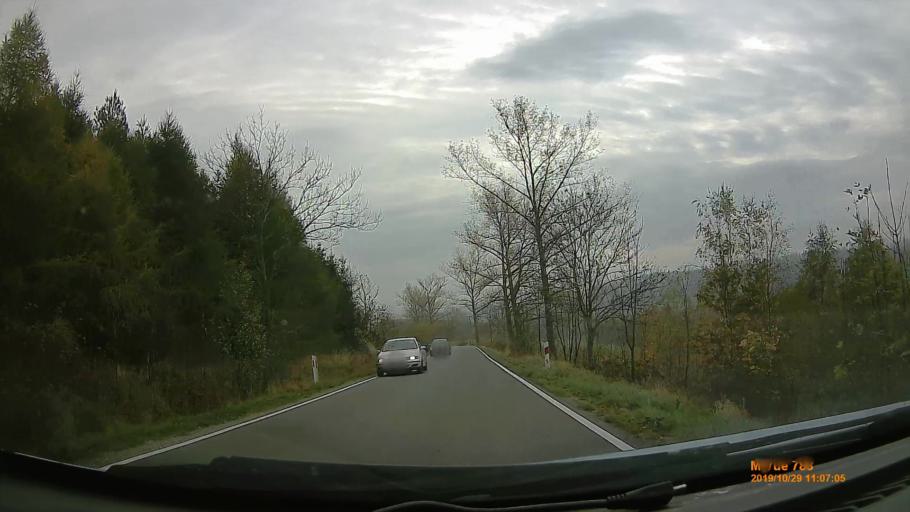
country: PL
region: Lower Silesian Voivodeship
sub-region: Powiat klodzki
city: Szczytna
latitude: 50.4596
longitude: 16.4845
